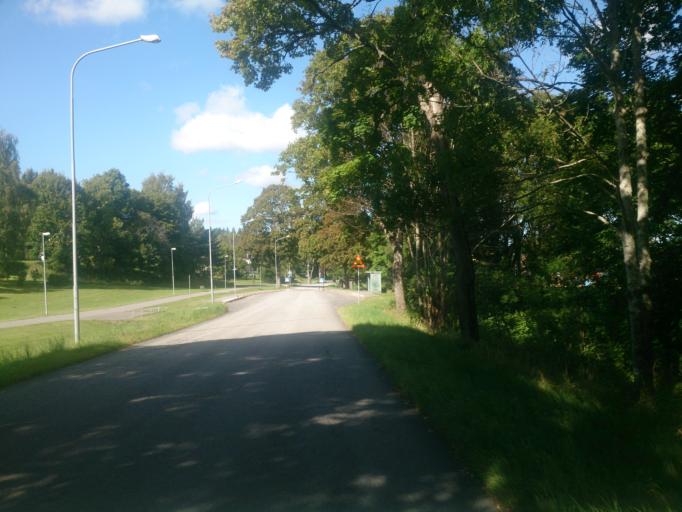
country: SE
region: OEstergoetland
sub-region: Atvidabergs Kommun
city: Atvidaberg
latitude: 58.2084
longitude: 15.9851
